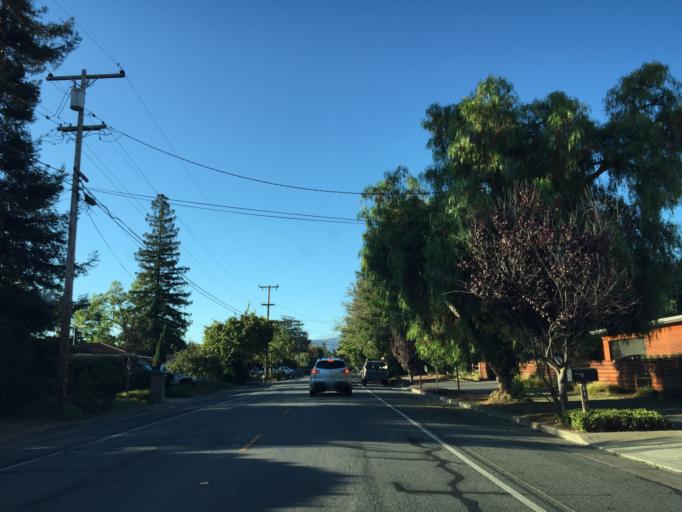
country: US
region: California
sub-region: Santa Clara County
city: Los Altos
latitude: 37.3980
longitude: -122.1213
